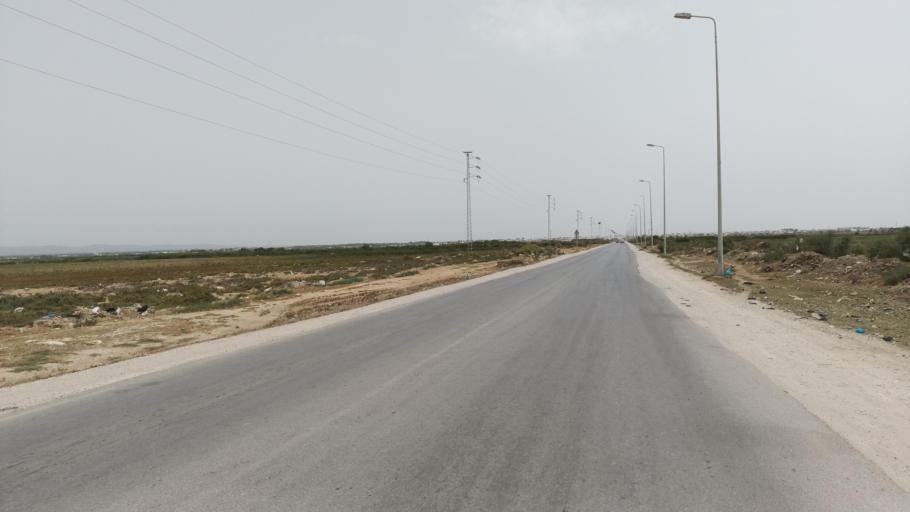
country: TN
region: Nabul
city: Manzil Bu Zalafah
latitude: 36.7257
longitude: 10.4704
